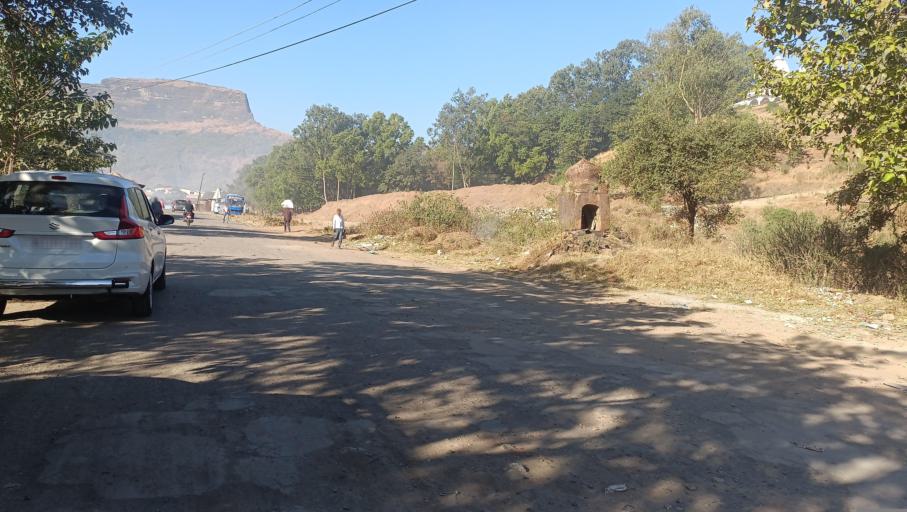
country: IN
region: Maharashtra
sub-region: Nashik Division
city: Trimbak
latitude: 19.9366
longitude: 73.5320
